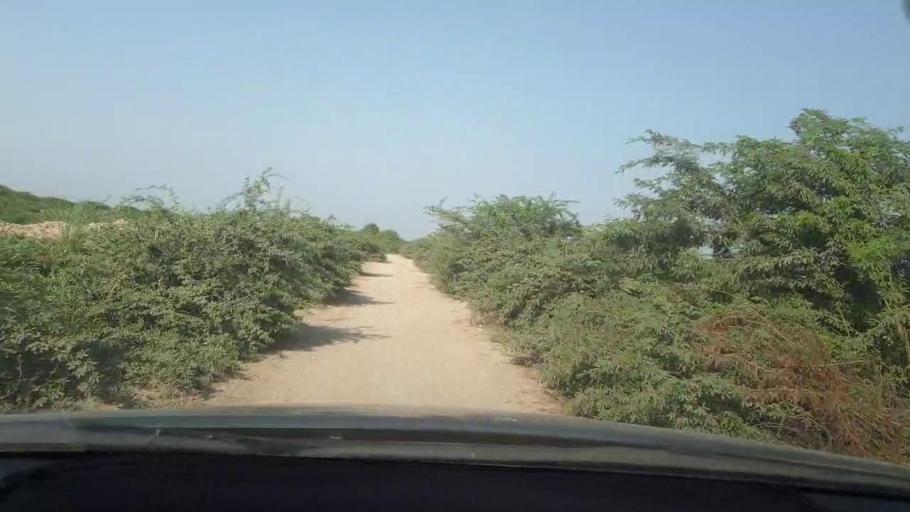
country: PK
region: Sindh
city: Naukot
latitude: 24.7762
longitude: 69.2607
